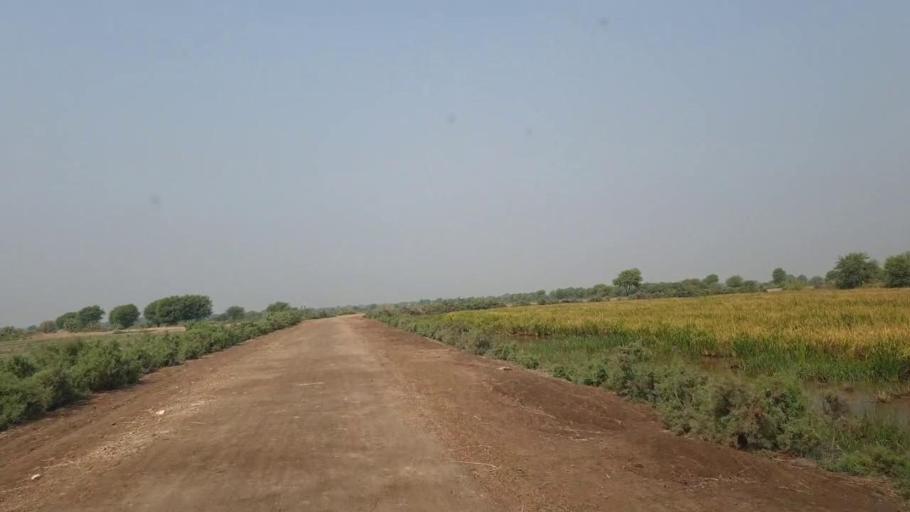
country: PK
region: Sindh
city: Matli
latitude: 25.1679
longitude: 68.7264
